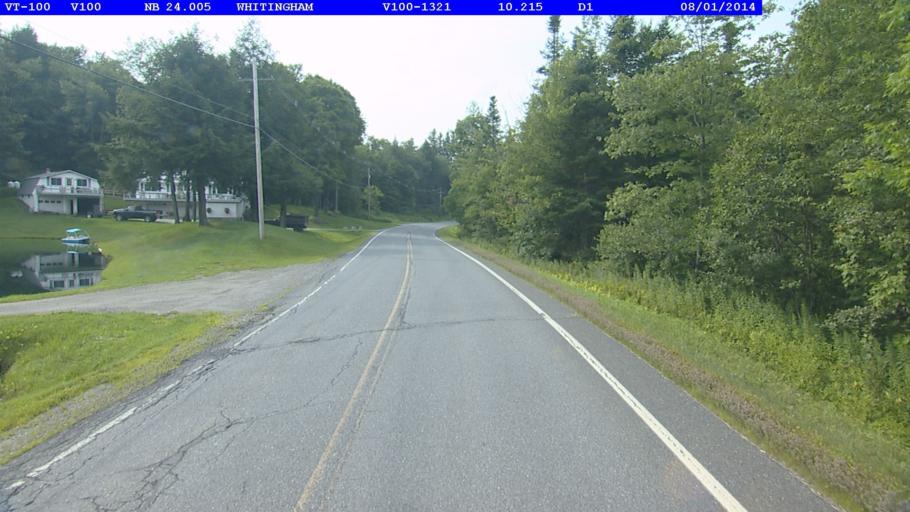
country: US
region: Vermont
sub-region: Windham County
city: Dover
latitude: 42.8217
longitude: -72.8569
